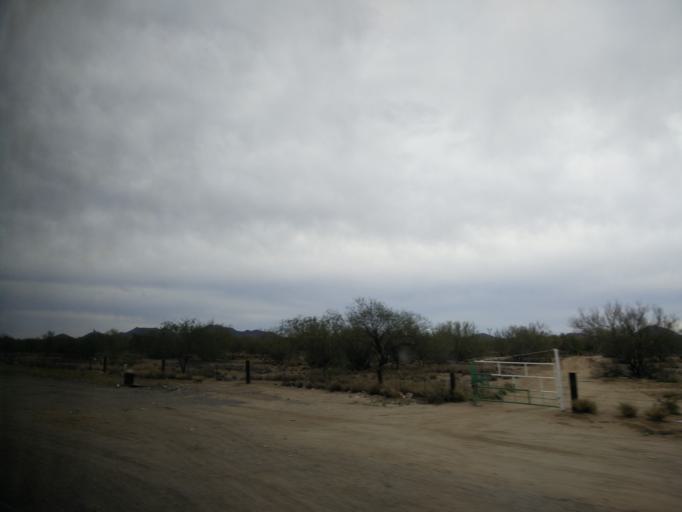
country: MX
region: Sonora
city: Hermosillo
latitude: 28.7338
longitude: -110.9774
